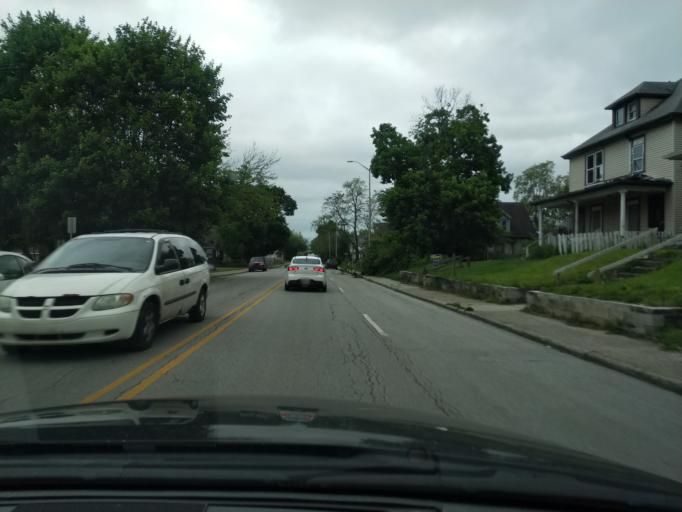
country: US
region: Indiana
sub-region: Marion County
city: Indianapolis
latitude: 39.8138
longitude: -86.1497
